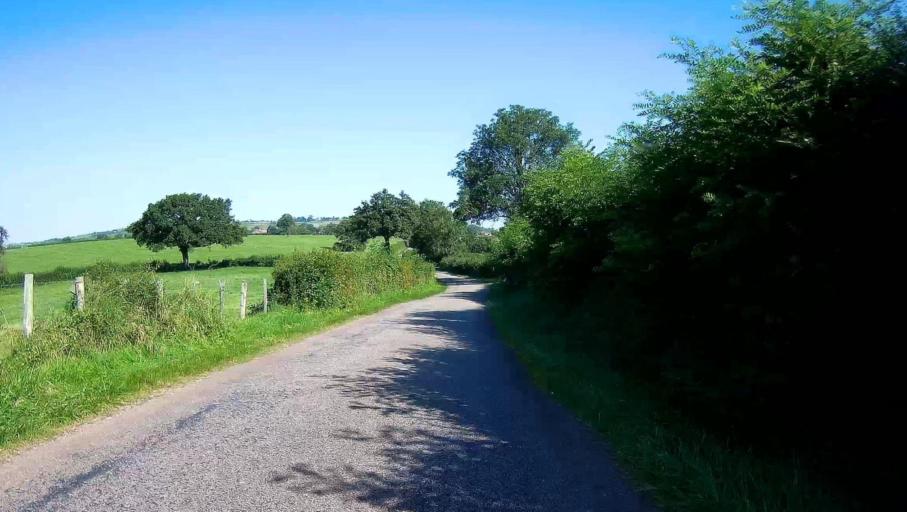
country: FR
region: Bourgogne
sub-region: Departement de Saone-et-Loire
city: Saint-Leger-sur-Dheune
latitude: 46.8294
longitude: 4.5938
